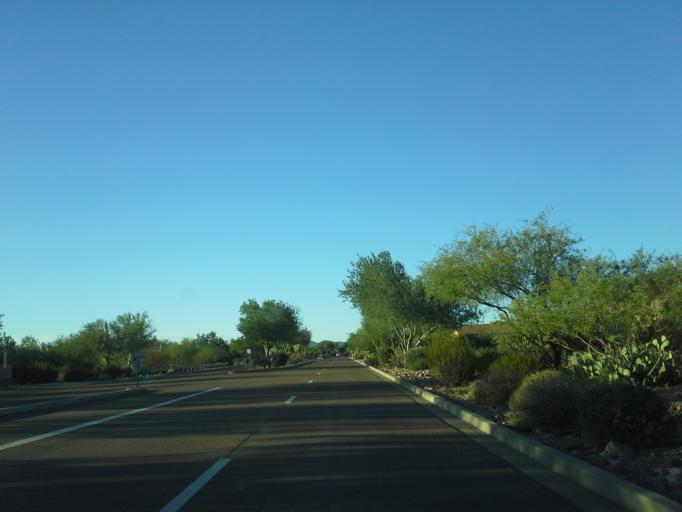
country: US
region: Arizona
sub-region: Pinal County
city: Apache Junction
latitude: 33.3762
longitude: -111.4691
